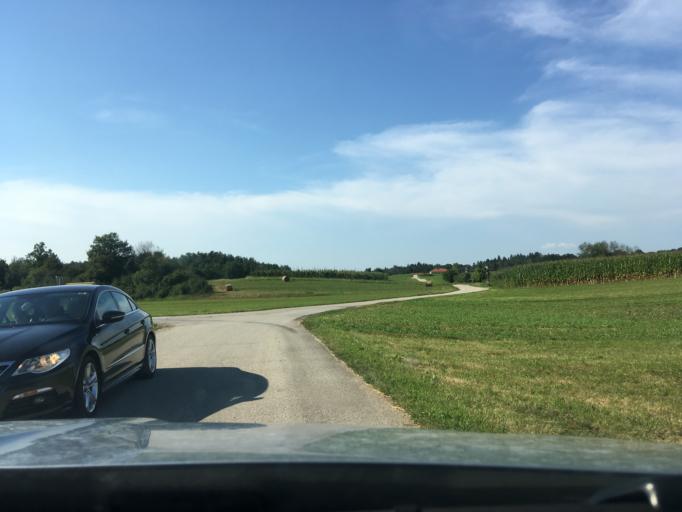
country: SI
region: Crnomelj
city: Crnomelj
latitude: 45.4736
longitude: 15.2084
